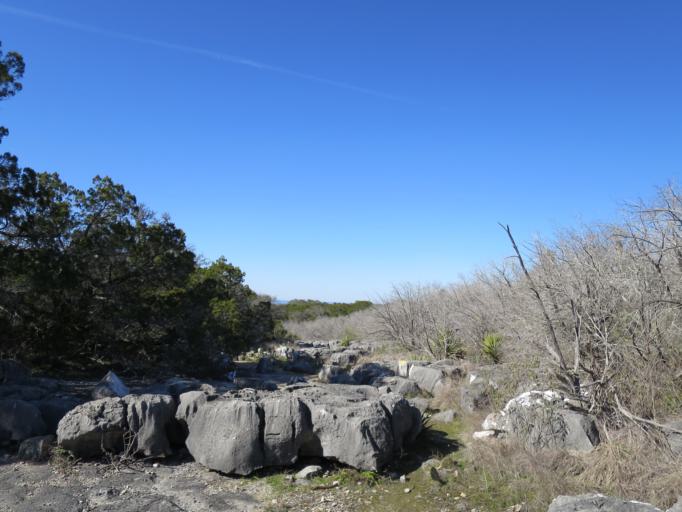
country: US
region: Texas
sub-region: Llano County
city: Kingsland
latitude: 30.6856
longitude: -98.3543
